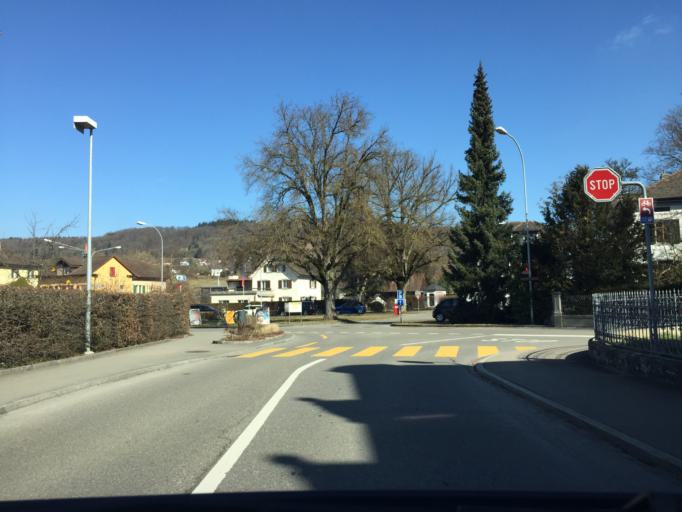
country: CH
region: Thurgau
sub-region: Frauenfeld District
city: Diessenhofen
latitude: 47.6876
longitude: 8.7539
